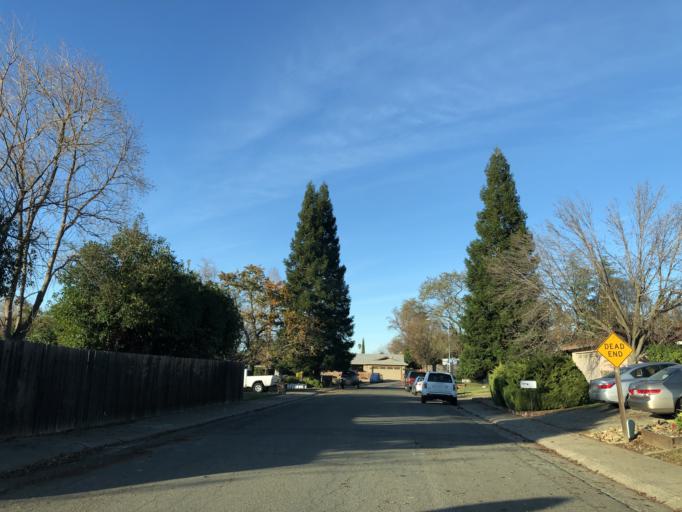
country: US
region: California
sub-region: Sacramento County
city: Foothill Farms
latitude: 38.6604
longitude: -121.3164
